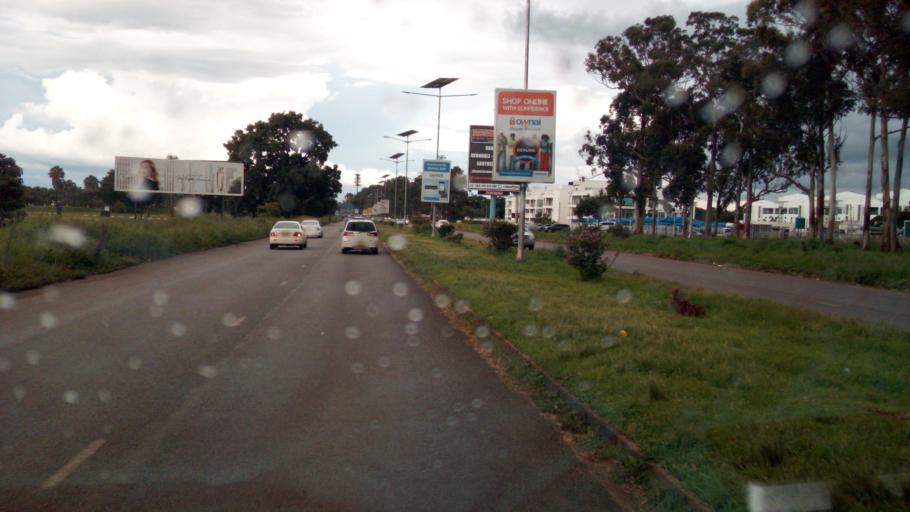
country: ZW
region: Harare
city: Harare
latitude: -17.7862
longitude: 31.0731
